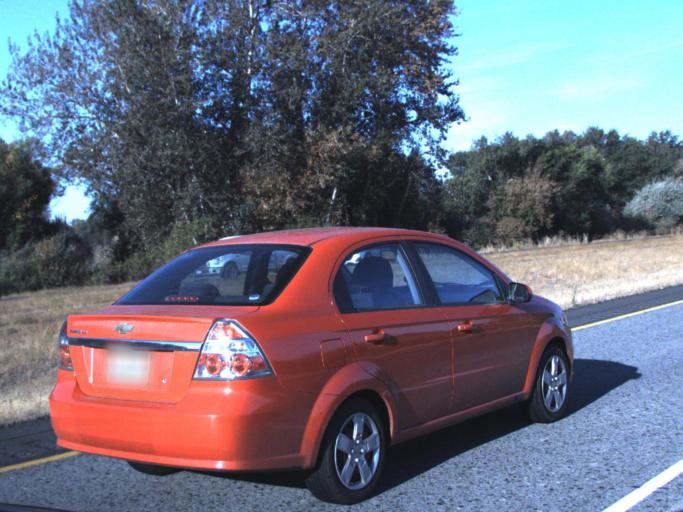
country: US
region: Washington
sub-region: Yakima County
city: Wapato
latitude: 46.4476
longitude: -120.3532
